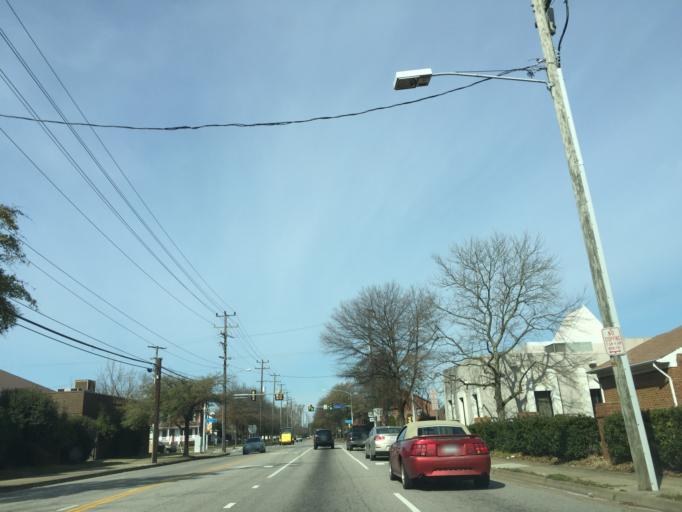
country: US
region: Virginia
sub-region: City of Norfolk
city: Norfolk
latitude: 36.8579
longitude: -76.2774
